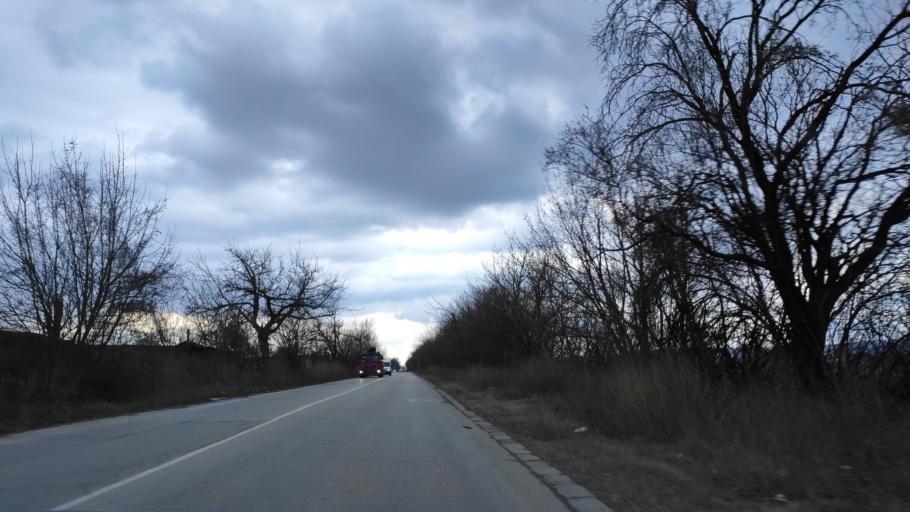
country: BG
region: Varna
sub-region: Obshtina Aksakovo
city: Aksakovo
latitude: 43.2279
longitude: 27.8482
